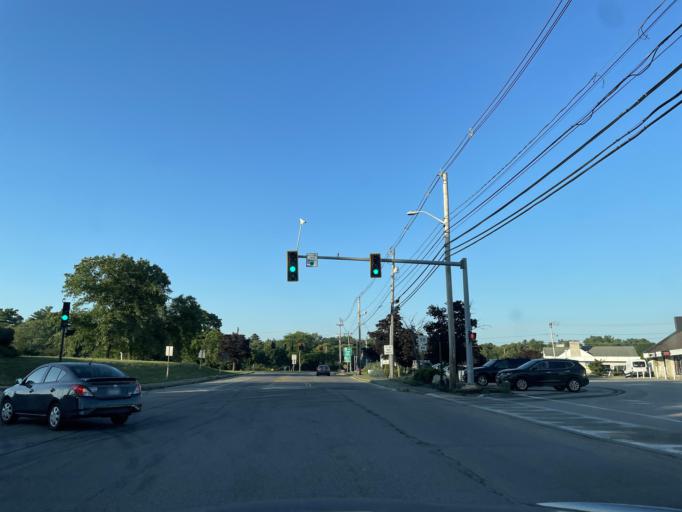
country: US
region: Massachusetts
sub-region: Plymouth County
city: Halifax
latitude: 41.9951
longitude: -70.8452
